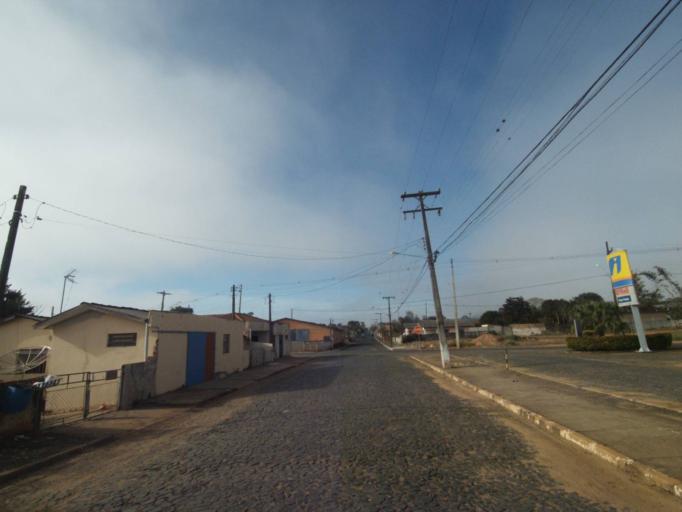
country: BR
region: Parana
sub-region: Tibagi
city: Tibagi
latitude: -24.5097
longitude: -50.4163
